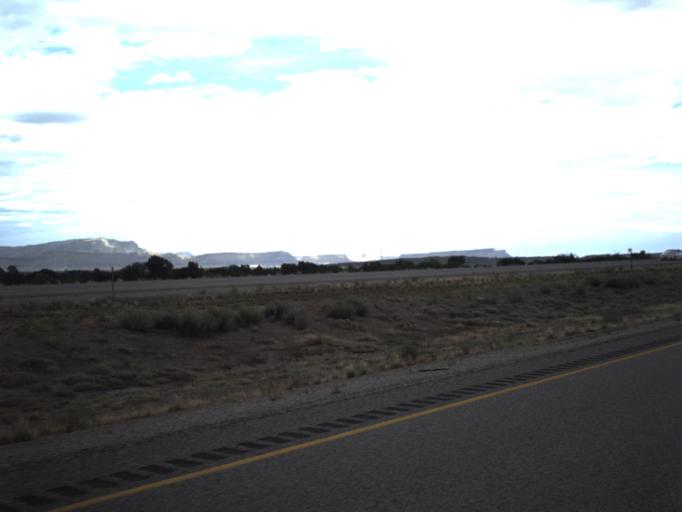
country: US
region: Utah
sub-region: Carbon County
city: East Carbon City
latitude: 38.9877
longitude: -110.1687
